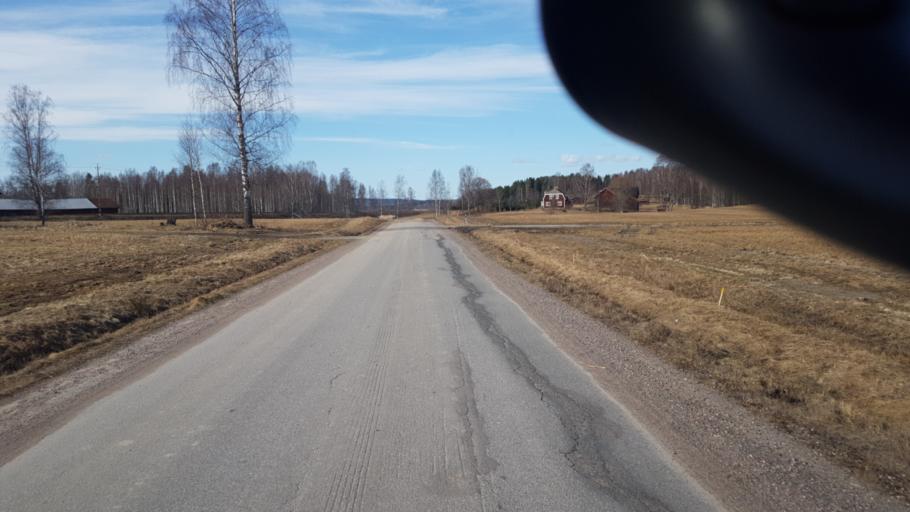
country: SE
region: Vaermland
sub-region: Eda Kommun
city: Amotfors
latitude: 59.7789
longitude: 12.3742
